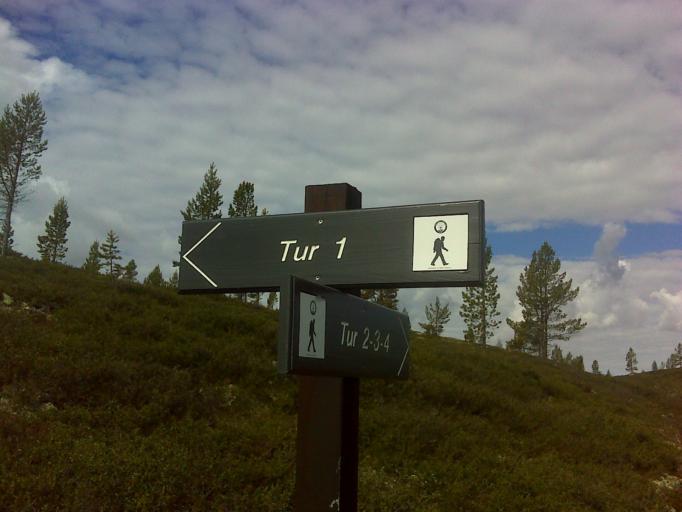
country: NO
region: Hedmark
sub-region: Folldal
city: Folldal
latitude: 62.1464
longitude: 10.0047
